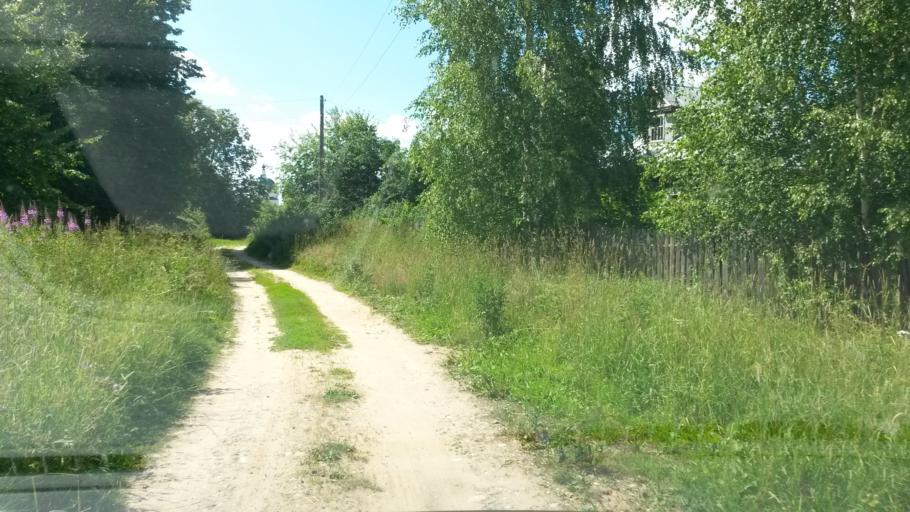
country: RU
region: Ivanovo
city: Zarechnyy
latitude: 57.4722
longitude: 42.3273
